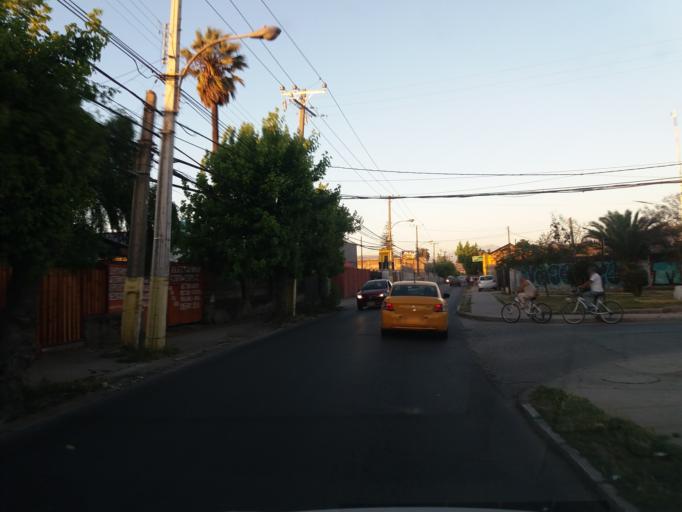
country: CL
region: Valparaiso
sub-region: Provincia de Quillota
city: Quillota
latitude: -32.8934
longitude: -71.2636
